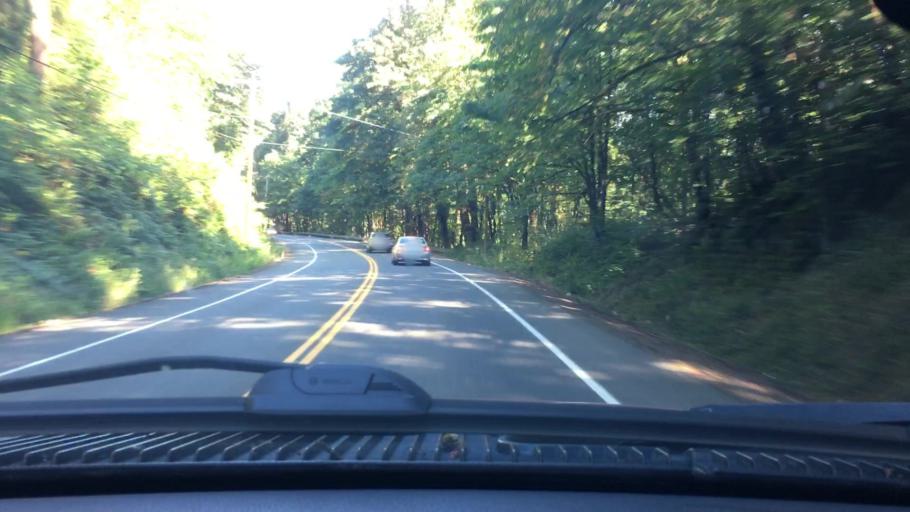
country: US
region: Washington
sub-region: King County
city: Lake Morton-Berrydale
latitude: 47.3356
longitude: -122.1231
